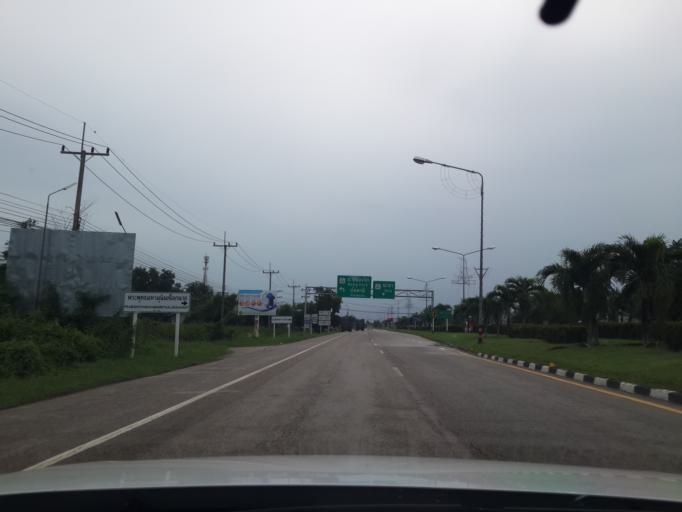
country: TH
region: Pattani
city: Nong Chik
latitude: 6.8021
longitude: 101.1490
